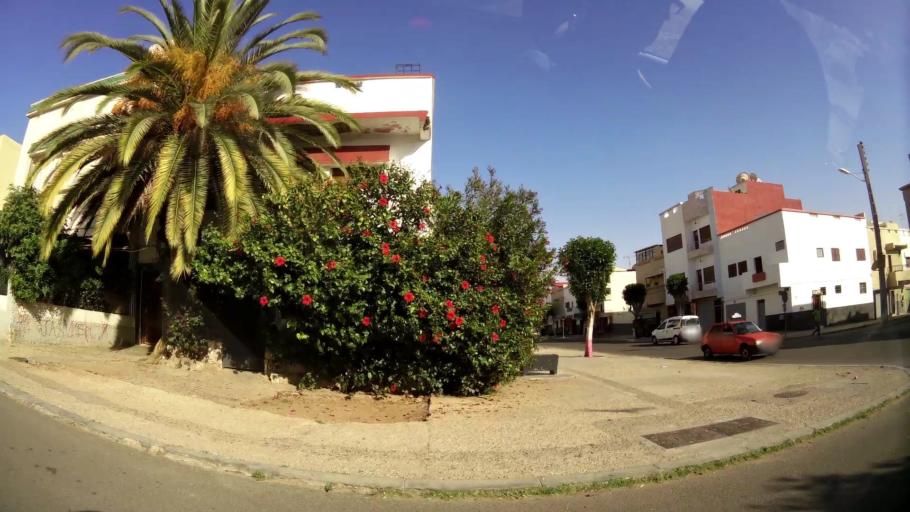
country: MA
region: Souss-Massa-Draa
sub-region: Agadir-Ida-ou-Tnan
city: Agadir
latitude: 30.4316
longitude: -9.5784
